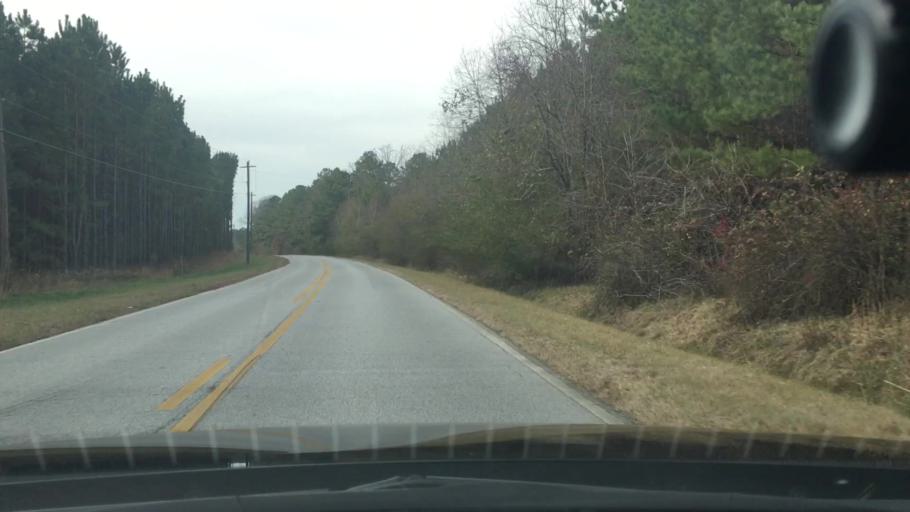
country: US
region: Georgia
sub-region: Spalding County
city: Experiment
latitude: 33.2721
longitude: -84.3513
